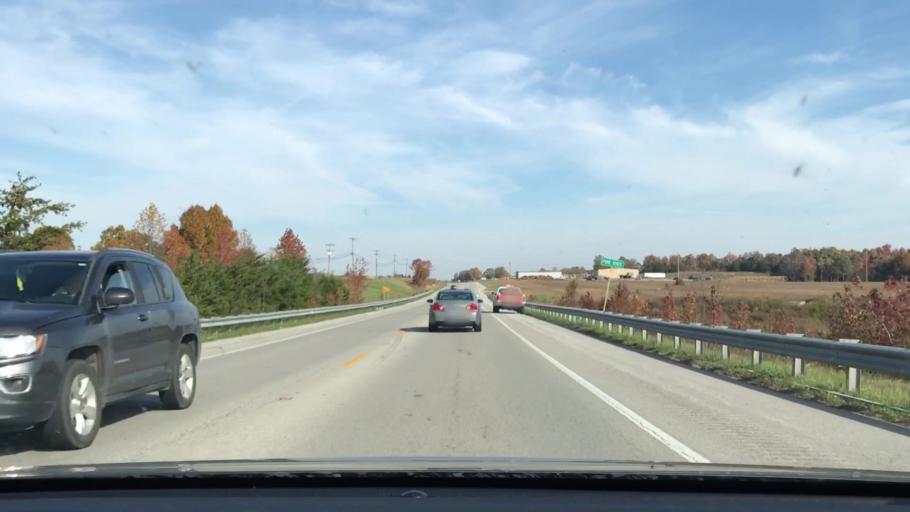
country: US
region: Kentucky
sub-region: McCreary County
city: Pine Knot
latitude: 36.6363
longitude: -84.4346
